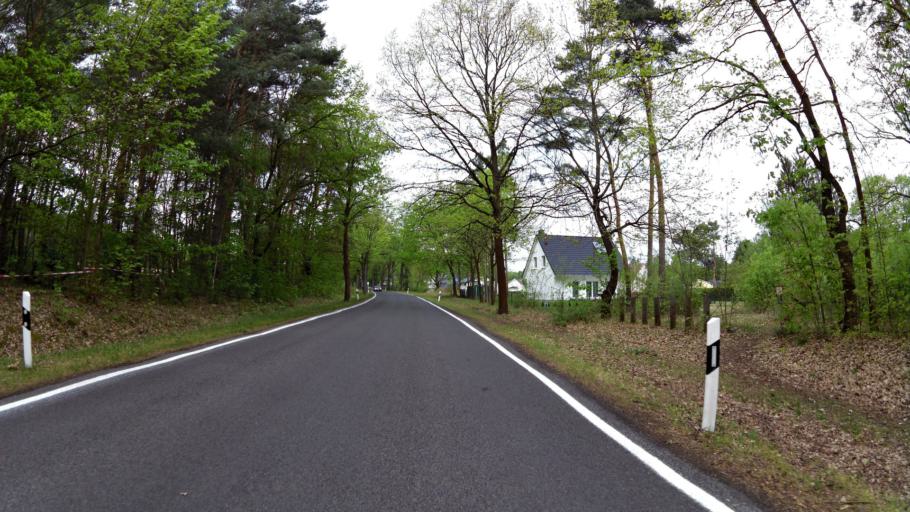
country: DE
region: Brandenburg
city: Mittenwalde
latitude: 52.2026
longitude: 13.5722
